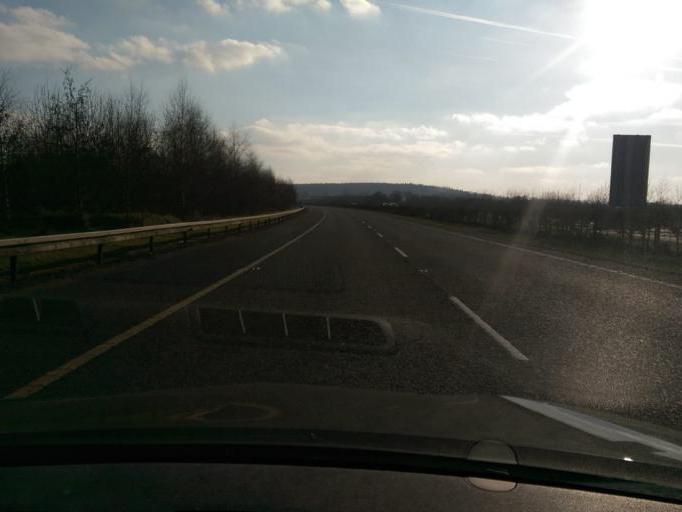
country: IE
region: Leinster
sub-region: Kildare
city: Monasterevin
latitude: 53.1409
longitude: -7.0289
